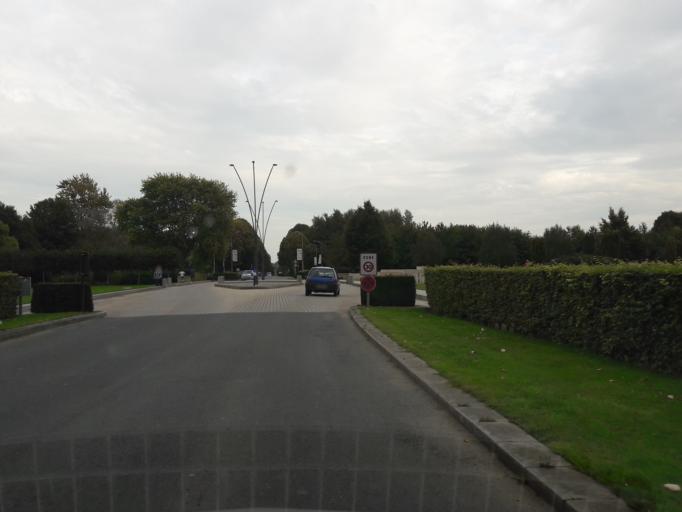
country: FR
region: Lower Normandy
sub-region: Departement du Calvados
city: Bayeux
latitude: 49.2746
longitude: -0.7145
